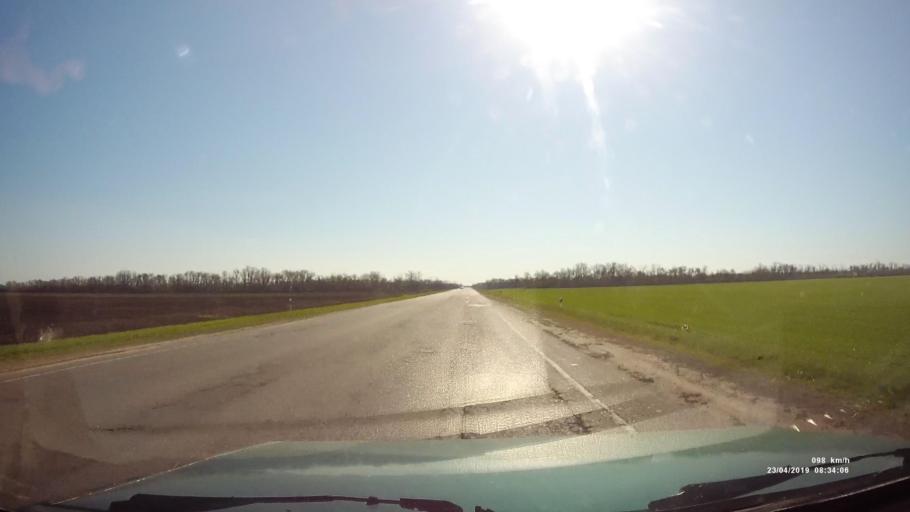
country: RU
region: Rostov
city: Tselina
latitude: 46.5245
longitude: 41.1060
